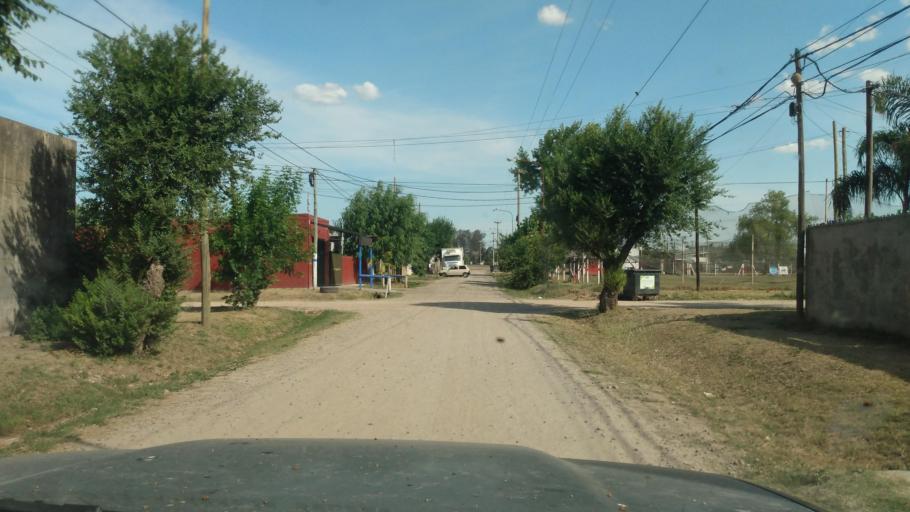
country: AR
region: Buenos Aires
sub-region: Partido de Lujan
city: Lujan
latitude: -34.5522
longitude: -59.1045
